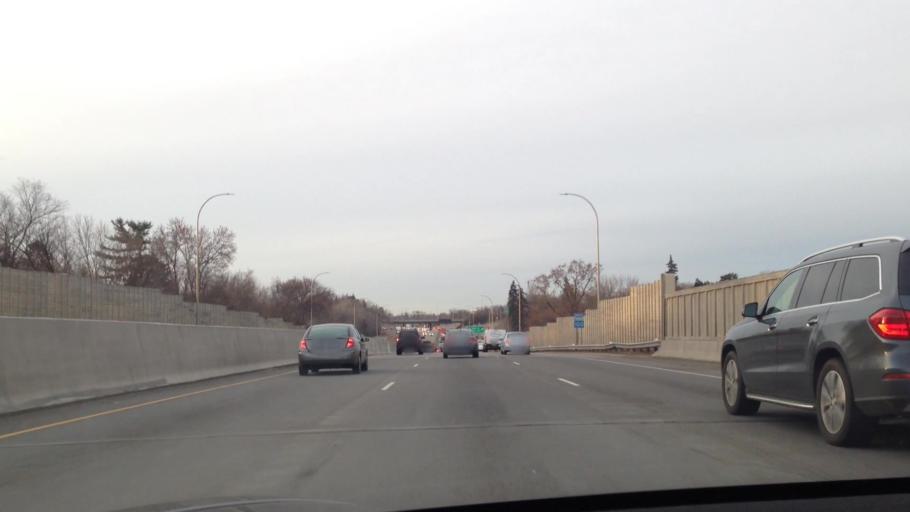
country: US
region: Minnesota
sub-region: Hennepin County
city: Edina
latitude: 44.9190
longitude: -93.3498
